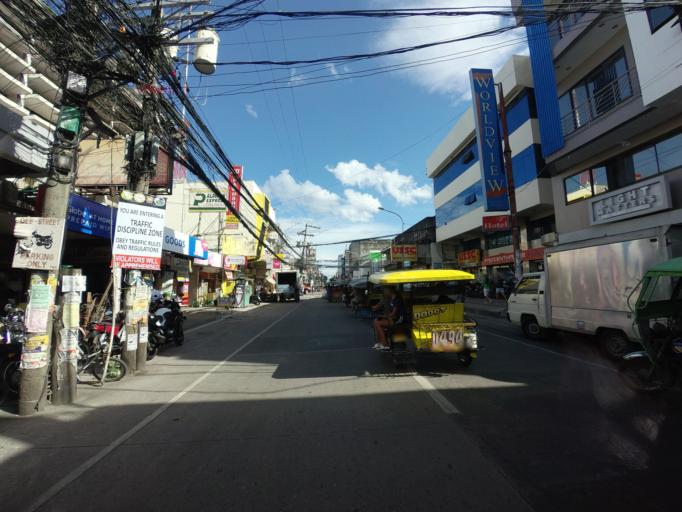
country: PH
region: Central Visayas
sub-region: Province of Negros Oriental
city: Dumaguete
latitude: 9.3079
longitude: 123.3083
